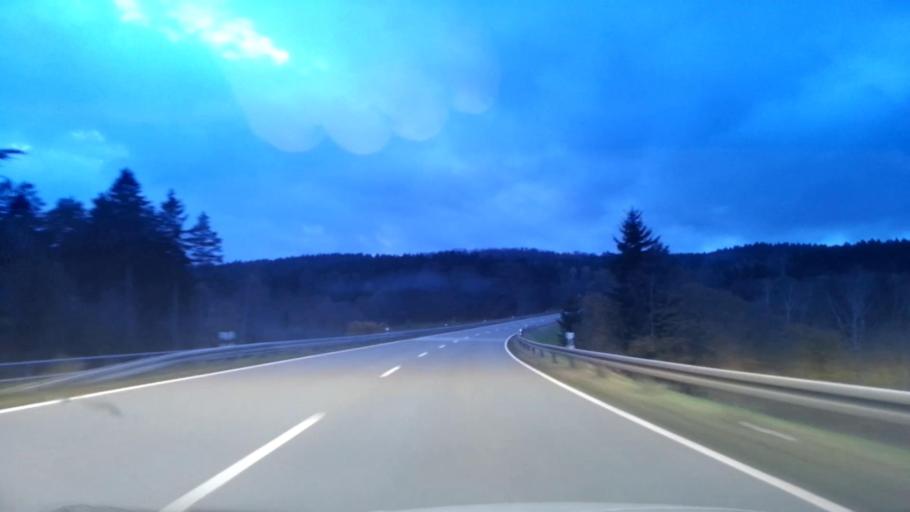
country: DE
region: Bavaria
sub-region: Upper Palatinate
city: Fuchsmuhl
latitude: 49.9301
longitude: 12.1363
